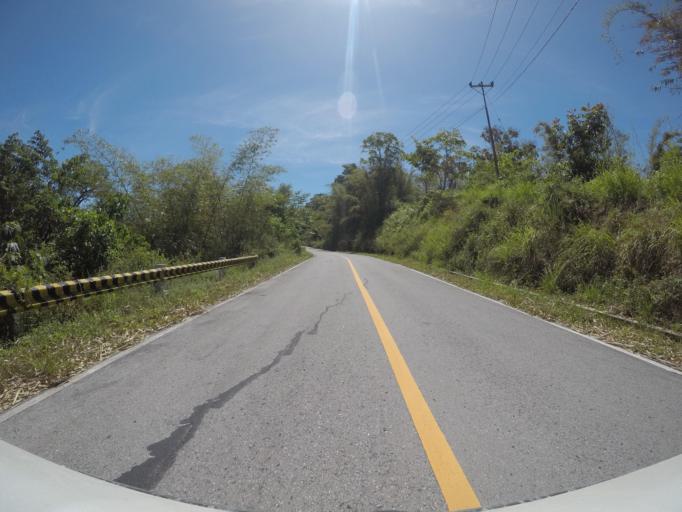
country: TL
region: Manatuto
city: Manatuto
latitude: -8.8768
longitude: 125.9919
